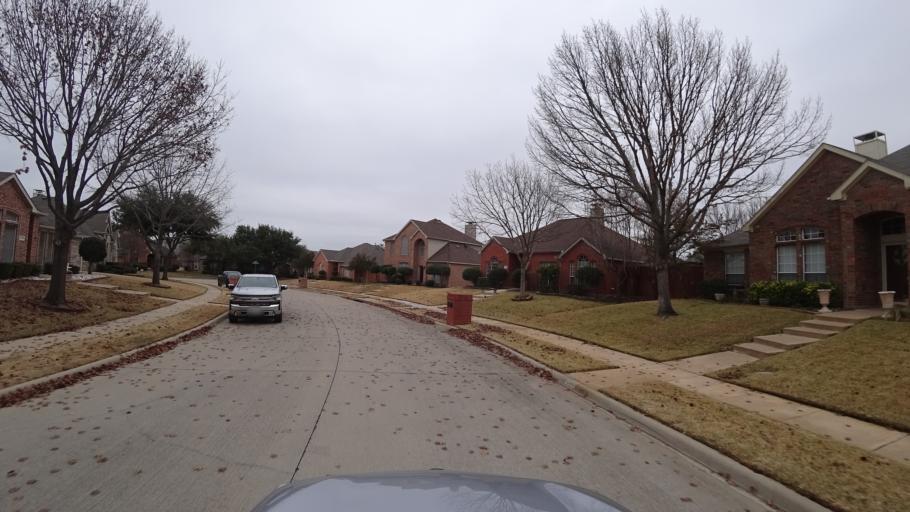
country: US
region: Texas
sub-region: Denton County
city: Highland Village
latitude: 33.0591
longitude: -97.0337
